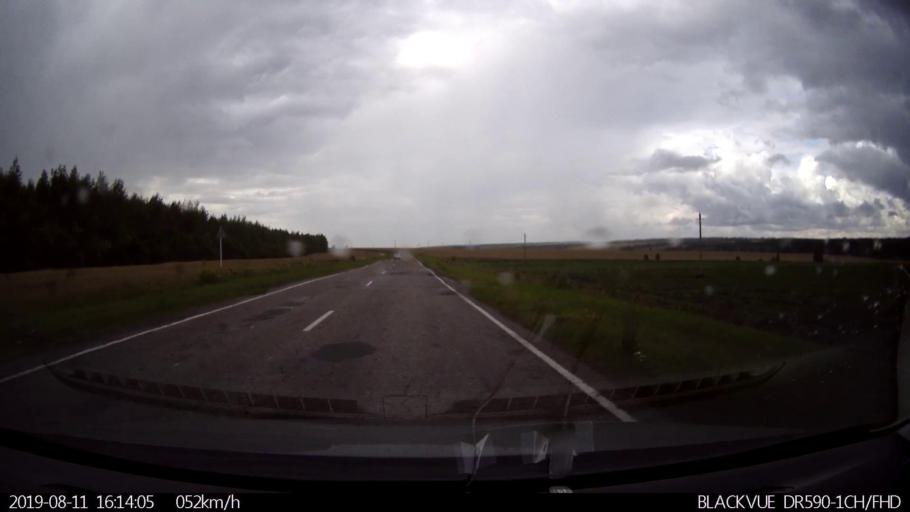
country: RU
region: Ulyanovsk
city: Ignatovka
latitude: 54.0252
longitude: 47.6349
